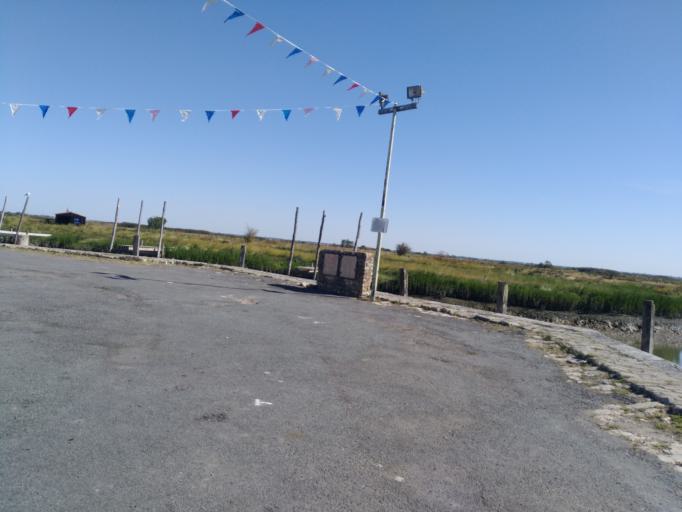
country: FR
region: Poitou-Charentes
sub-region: Departement de la Charente-Maritime
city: Breuillet
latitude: 45.7113
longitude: -1.0272
